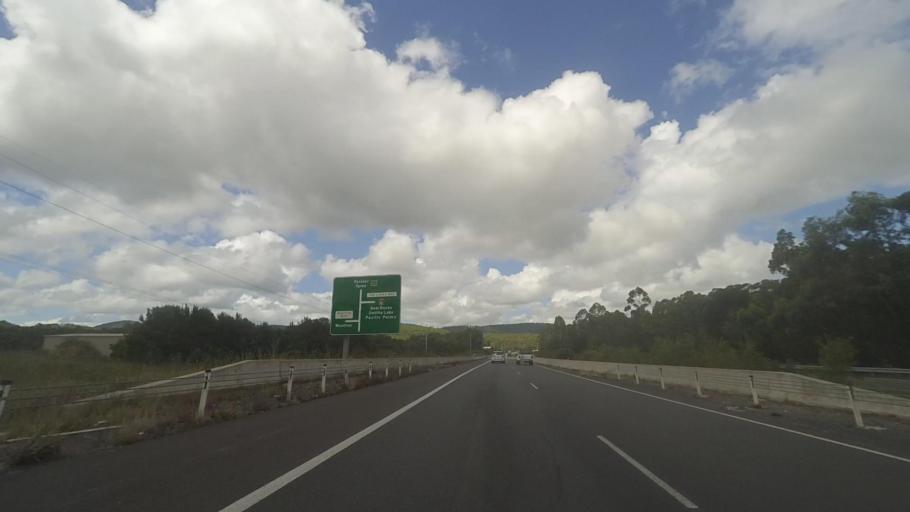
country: AU
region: New South Wales
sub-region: Great Lakes
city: Bulahdelah
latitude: -32.3891
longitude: 152.2240
